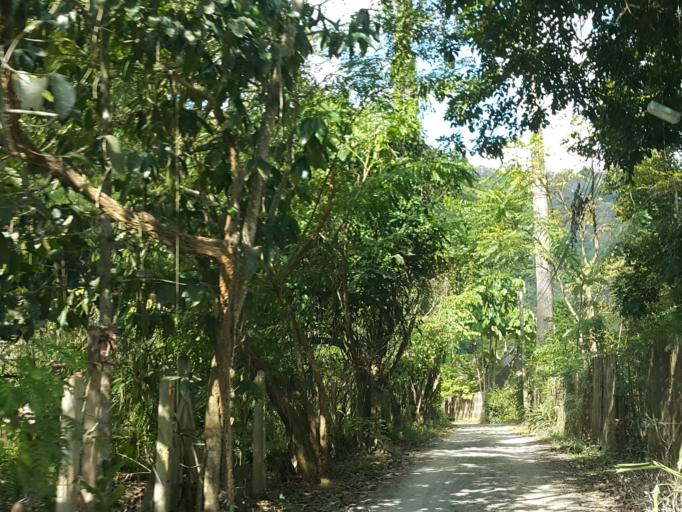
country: TH
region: Chiang Mai
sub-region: Amphoe Chiang Dao
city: Chiang Dao
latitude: 19.4038
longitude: 98.9257
